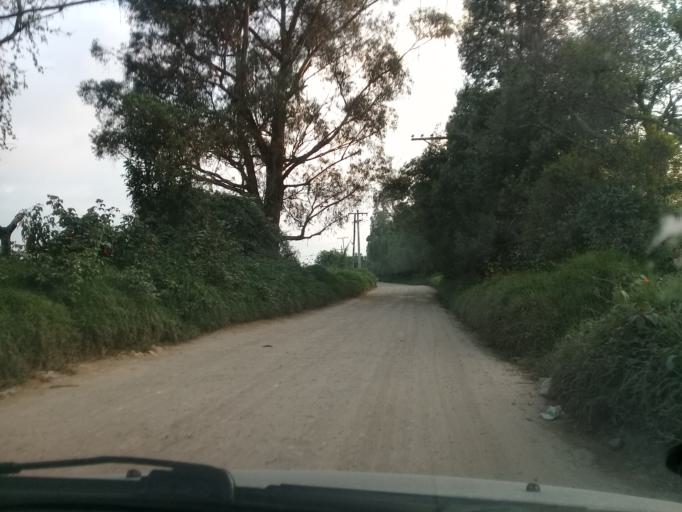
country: CO
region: Cundinamarca
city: El Rosal
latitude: 4.7920
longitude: -74.2268
